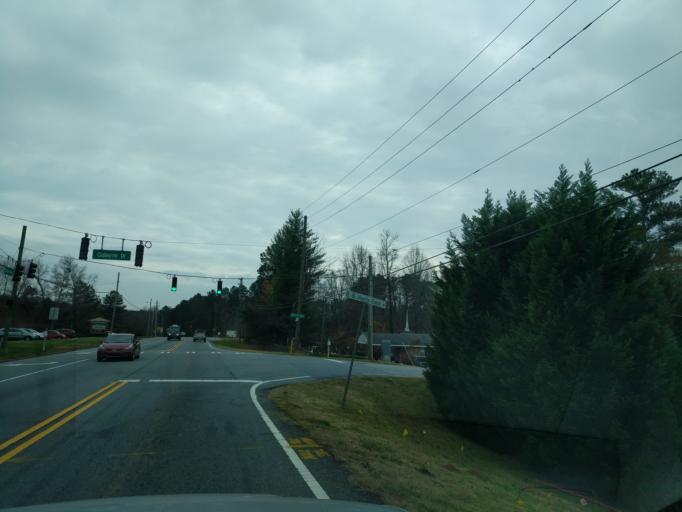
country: US
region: Georgia
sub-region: Gwinnett County
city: Duluth
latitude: 33.9878
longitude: -84.1312
